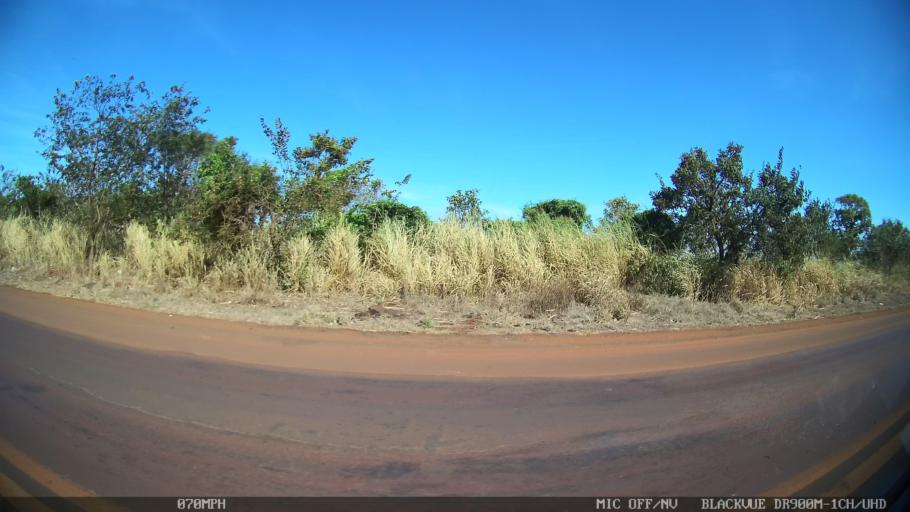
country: BR
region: Sao Paulo
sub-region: Sao Joaquim Da Barra
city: Sao Joaquim da Barra
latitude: -20.5112
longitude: -47.9057
